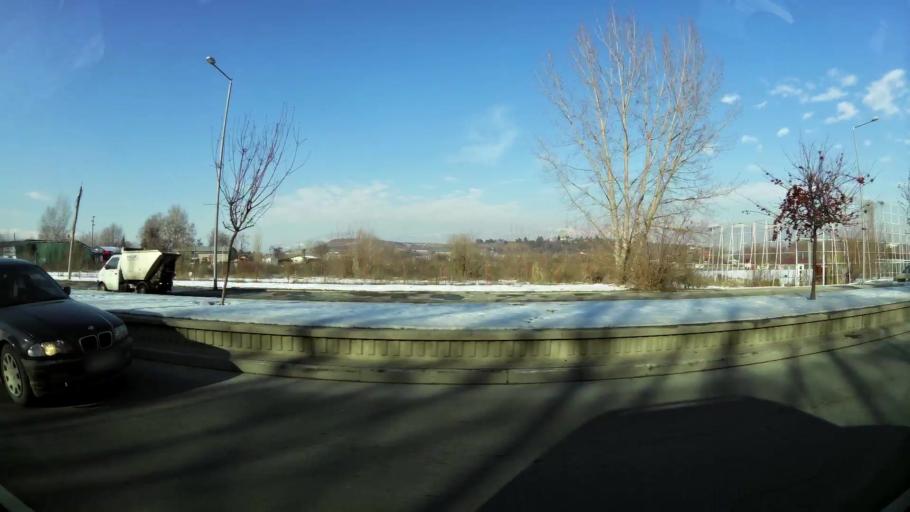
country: MK
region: Karpos
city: Skopje
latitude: 42.0074
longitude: 21.3975
